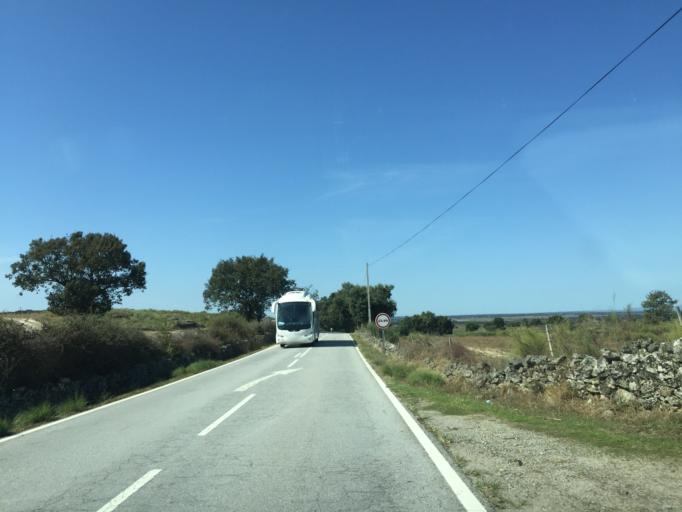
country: PT
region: Portalegre
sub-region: Portalegre
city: Alagoa
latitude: 39.4392
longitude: -7.5545
